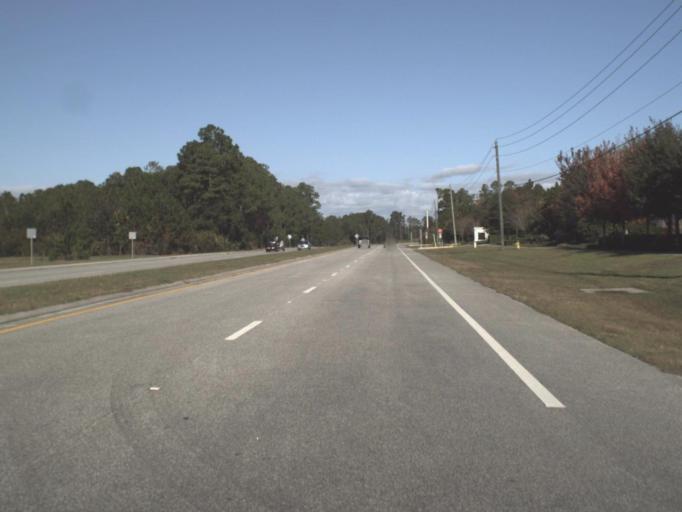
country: US
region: Florida
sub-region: Volusia County
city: Holly Hill
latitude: 29.2391
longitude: -81.0916
